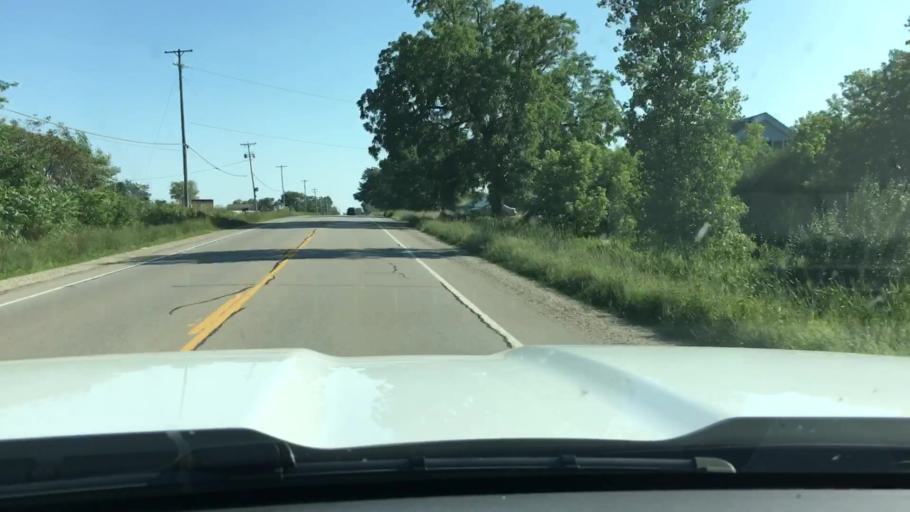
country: US
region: Michigan
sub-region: Ottawa County
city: Coopersville
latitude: 43.0417
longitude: -85.9567
